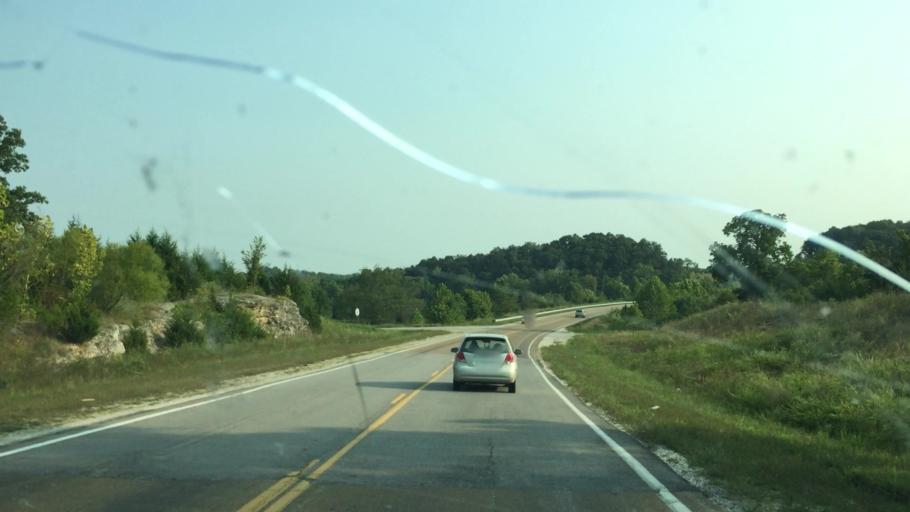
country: US
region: Missouri
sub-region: Pulaski County
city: Richland
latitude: 37.8051
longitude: -92.4053
